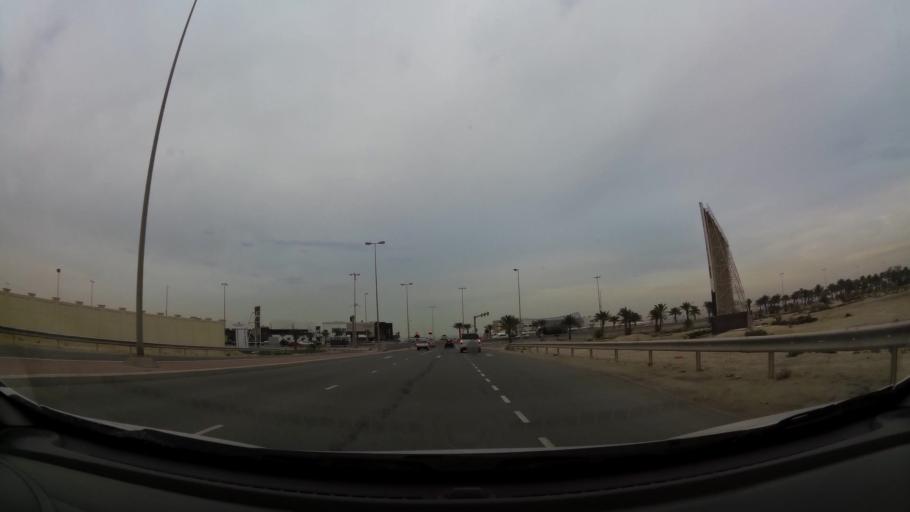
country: BH
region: Northern
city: Ar Rifa'
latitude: 26.1004
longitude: 50.5544
